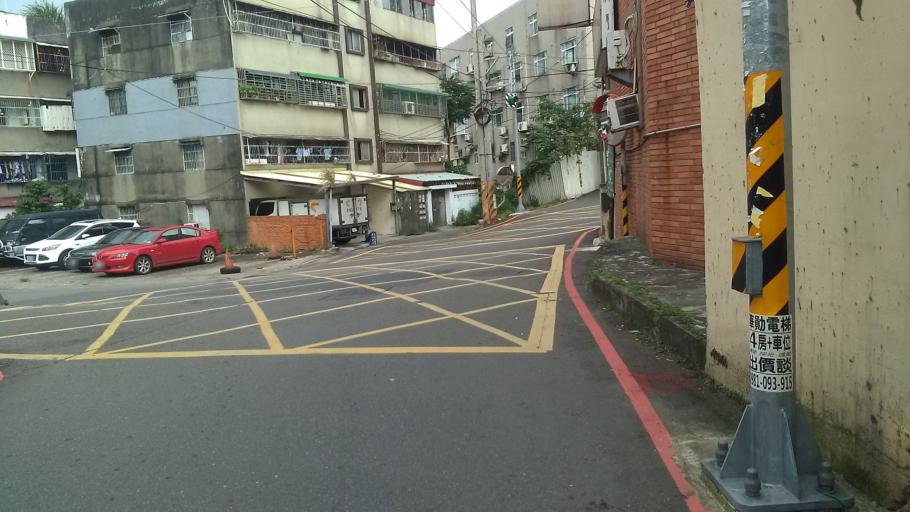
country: TW
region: Taiwan
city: Taoyuan City
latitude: 24.9512
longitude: 121.2606
